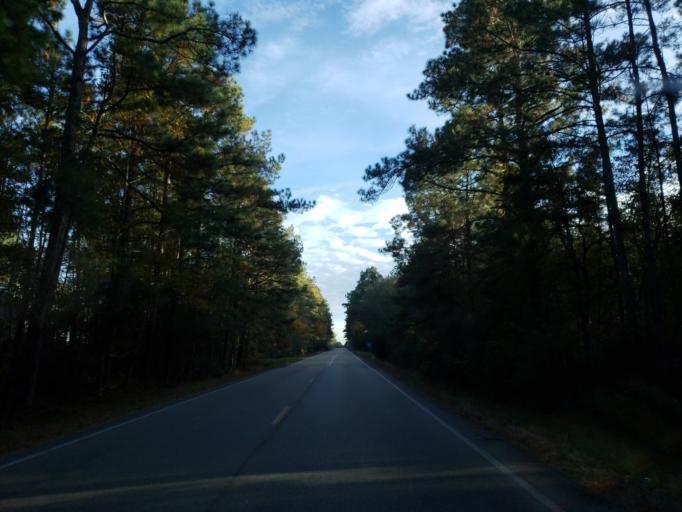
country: US
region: Mississippi
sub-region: Lamar County
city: Purvis
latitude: 31.1834
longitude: -89.4358
